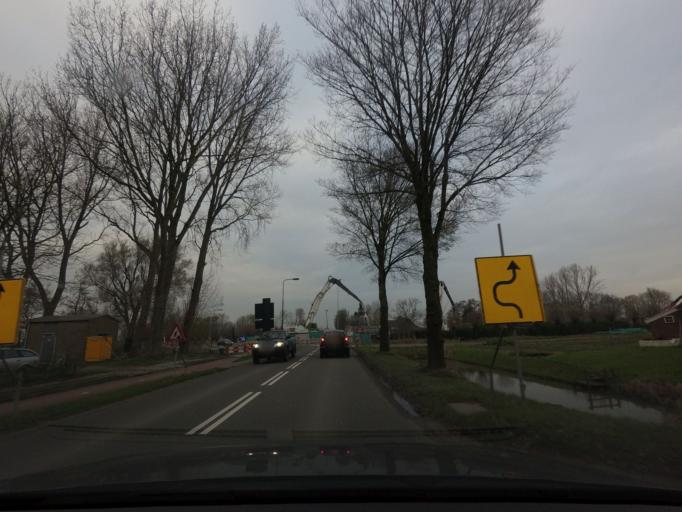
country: NL
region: North Holland
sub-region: Gemeente Heerhugowaard
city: Heerhugowaard
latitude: 52.6835
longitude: 4.8498
